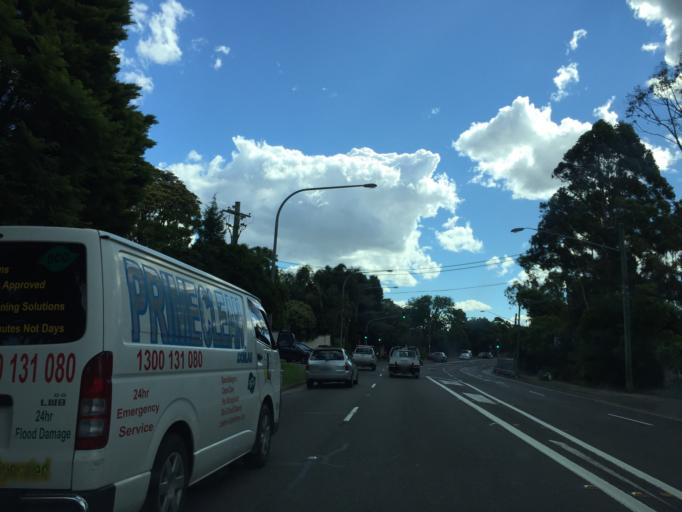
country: AU
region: New South Wales
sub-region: Parramatta
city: Telopea
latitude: -33.7859
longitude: 151.0389
